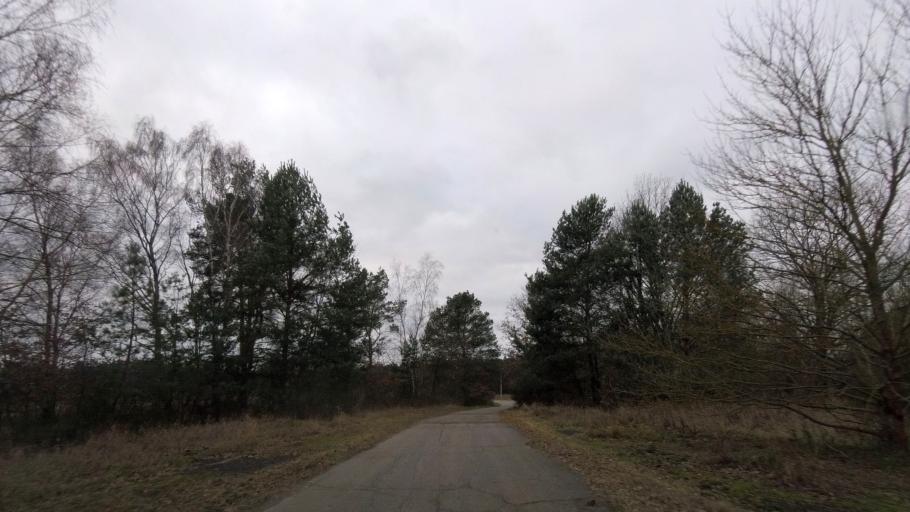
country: DE
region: Brandenburg
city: Niedergorsdorf
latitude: 51.9889
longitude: 12.9908
